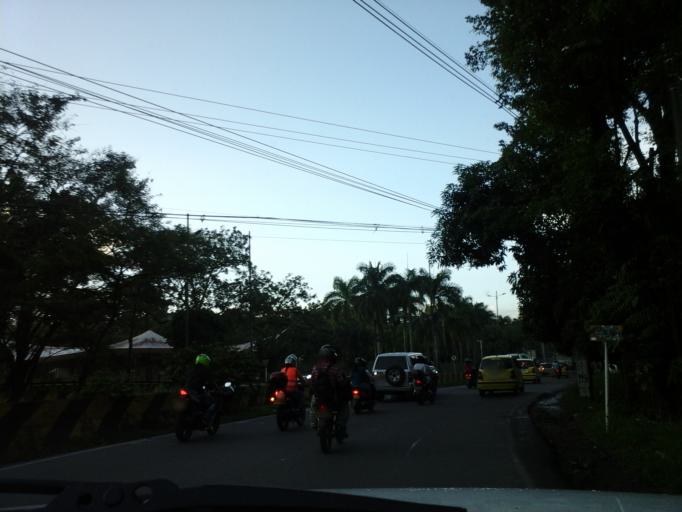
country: CO
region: Meta
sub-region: Villavicencio
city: Villavicencio
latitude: 4.1208
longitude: -73.6418
